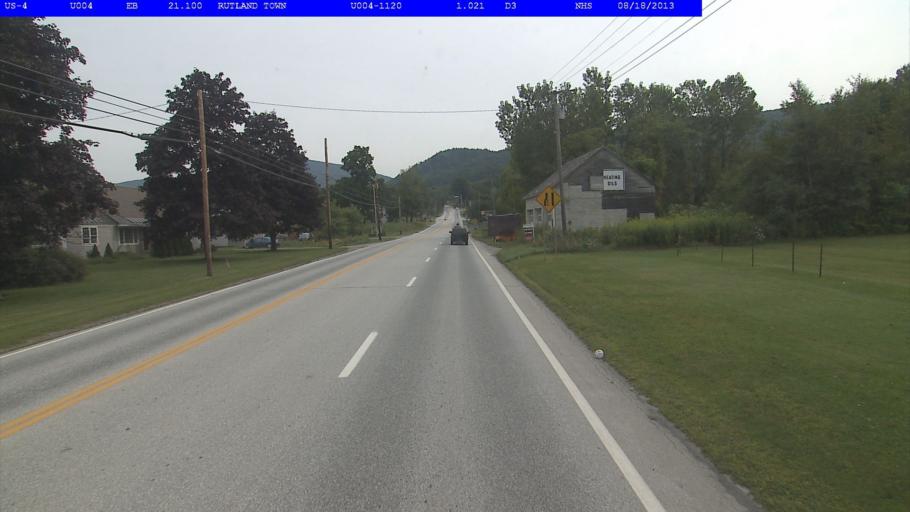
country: US
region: Vermont
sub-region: Rutland County
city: Rutland
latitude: 43.6327
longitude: -72.9405
